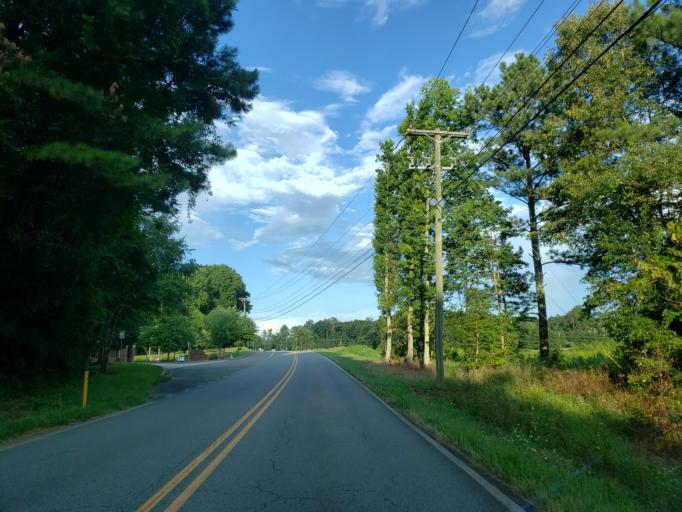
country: US
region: Georgia
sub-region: Cherokee County
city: Canton
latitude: 34.3303
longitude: -84.4913
